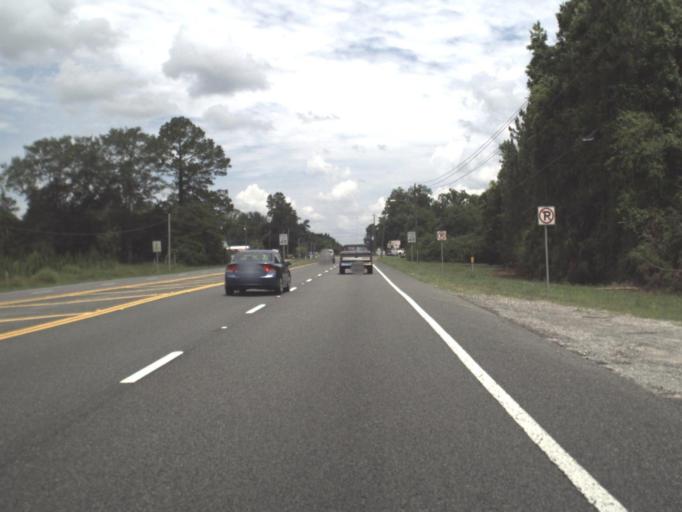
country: US
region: Florida
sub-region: Nassau County
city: Hilliard
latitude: 30.6807
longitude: -81.9105
